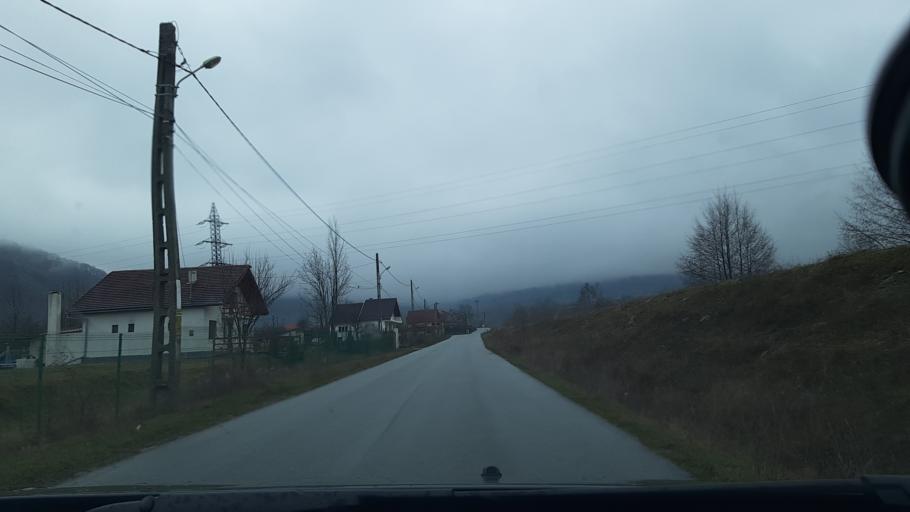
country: RO
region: Hunedoara
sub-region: Oras Petrila
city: Petrila
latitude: 45.4283
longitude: 23.4222
